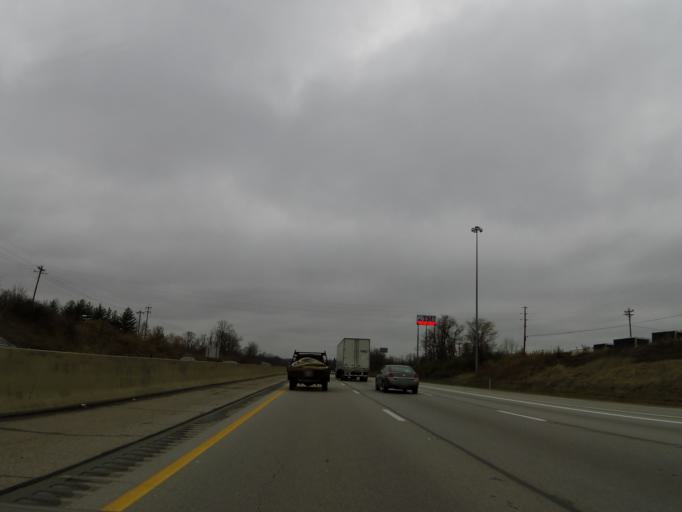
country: US
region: Kentucky
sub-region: Boone County
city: Walton
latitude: 38.8562
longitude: -84.6228
